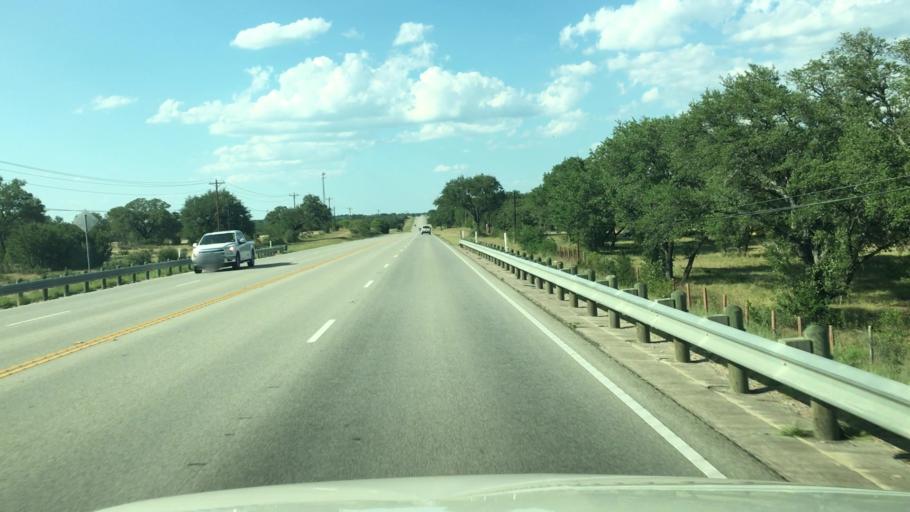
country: US
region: Texas
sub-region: Blanco County
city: Johnson City
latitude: 30.3246
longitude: -98.3878
